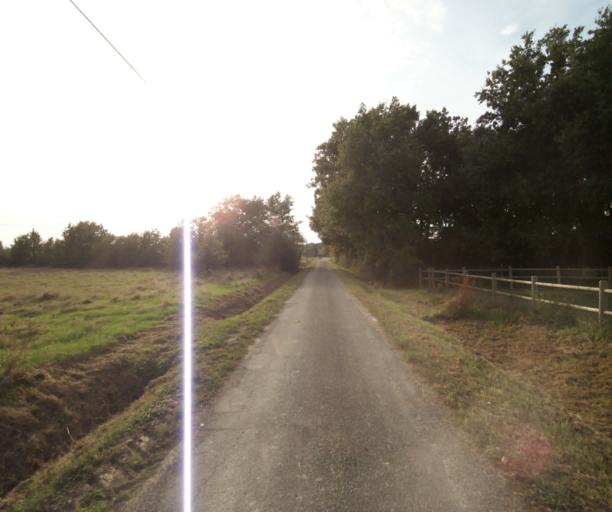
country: FR
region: Midi-Pyrenees
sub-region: Departement du Tarn-et-Garonne
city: Campsas
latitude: 43.8767
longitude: 1.3433
